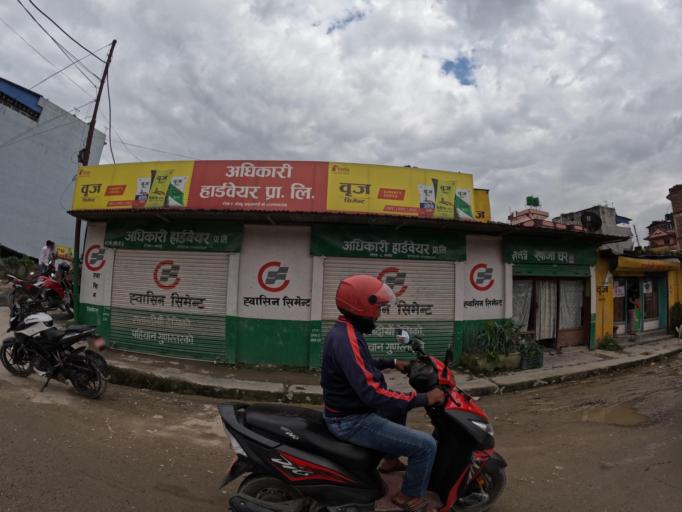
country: NP
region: Central Region
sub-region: Bagmati Zone
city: Kathmandu
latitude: 27.7417
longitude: 85.3139
